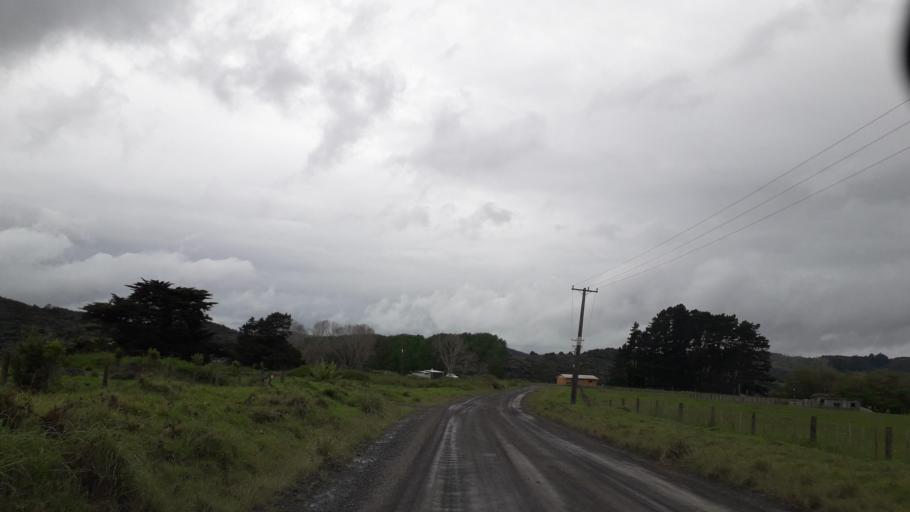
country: NZ
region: Northland
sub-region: Far North District
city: Kaitaia
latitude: -35.4055
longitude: 173.3664
